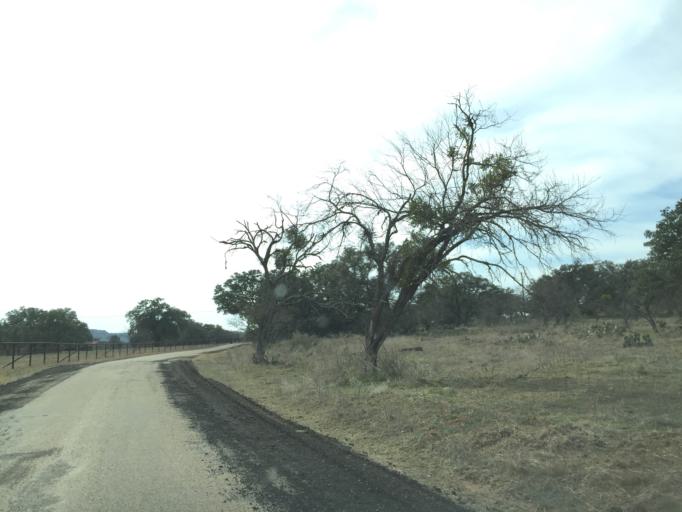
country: US
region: Texas
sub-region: Llano County
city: Kingsland
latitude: 30.4568
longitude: -98.6403
